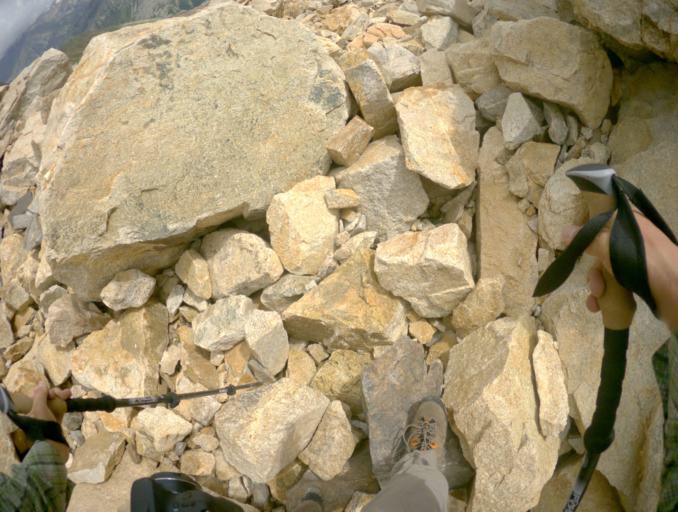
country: RU
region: Karachayevo-Cherkesiya
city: Uchkulan
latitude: 43.2764
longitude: 42.1198
